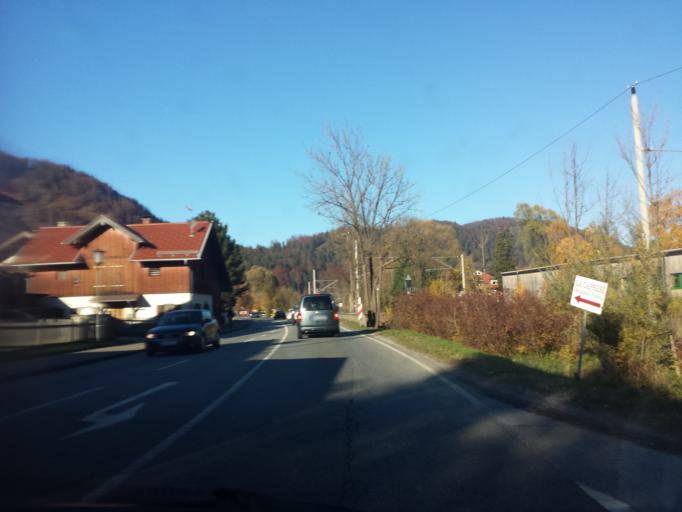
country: DE
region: Bavaria
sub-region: Upper Bavaria
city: Oberau
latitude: 47.5610
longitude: 11.1388
